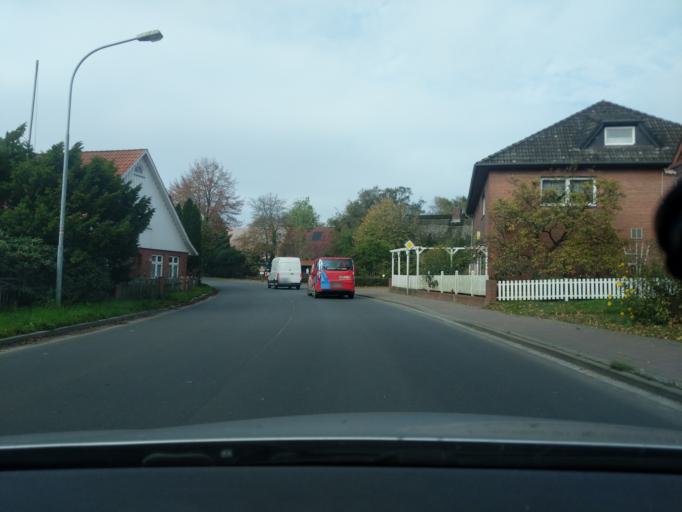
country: DE
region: Lower Saxony
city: Belum
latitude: 53.8168
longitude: 8.9938
